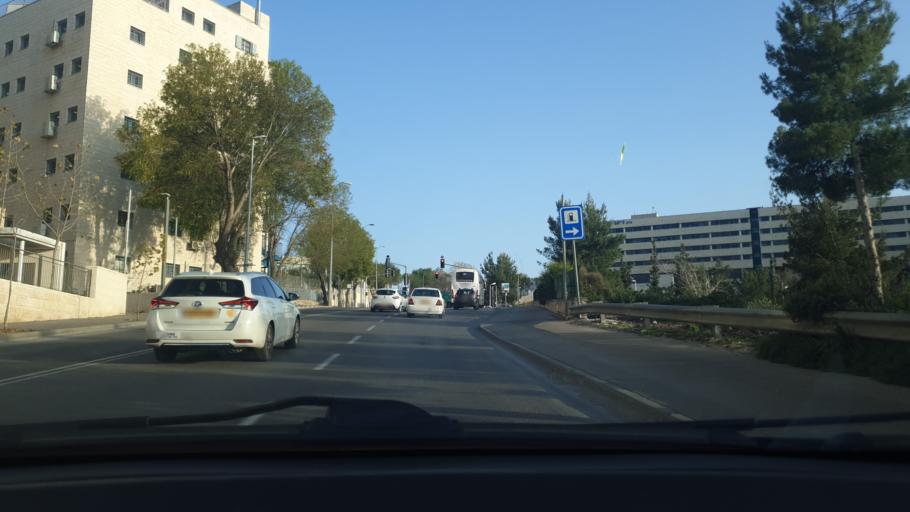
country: PS
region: West Bank
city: Bayt Iksa
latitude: 31.7901
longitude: 35.1887
